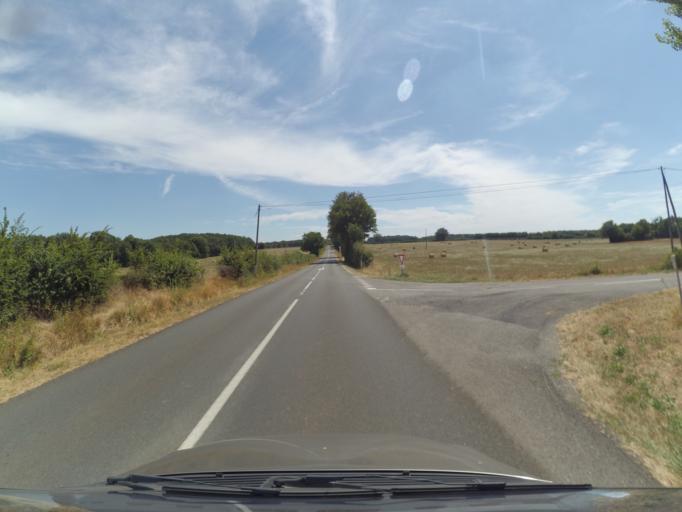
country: FR
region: Poitou-Charentes
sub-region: Departement de la Vienne
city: Usson-du-Poitou
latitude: 46.2883
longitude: 0.5118
